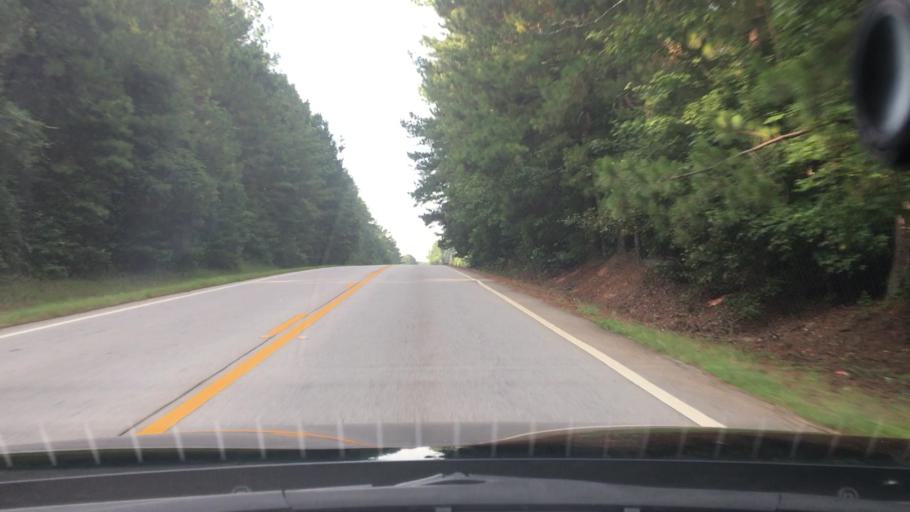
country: US
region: Georgia
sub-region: Fayette County
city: Peachtree City
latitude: 33.3834
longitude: -84.6256
